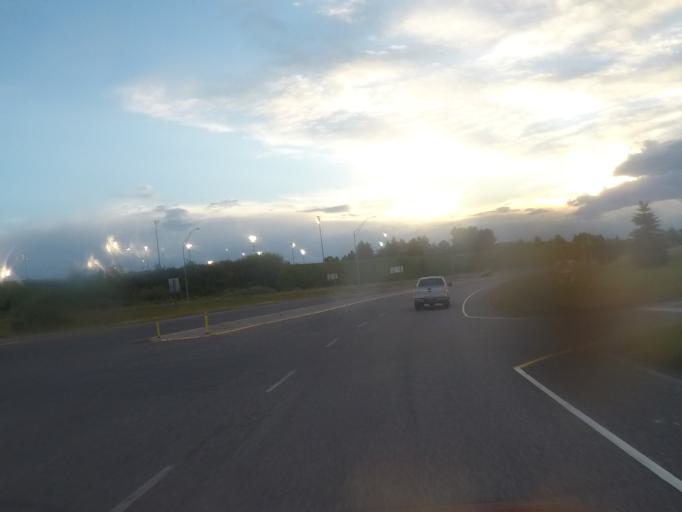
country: US
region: Montana
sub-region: Gallatin County
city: Bozeman
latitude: 45.6753
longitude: -111.0119
